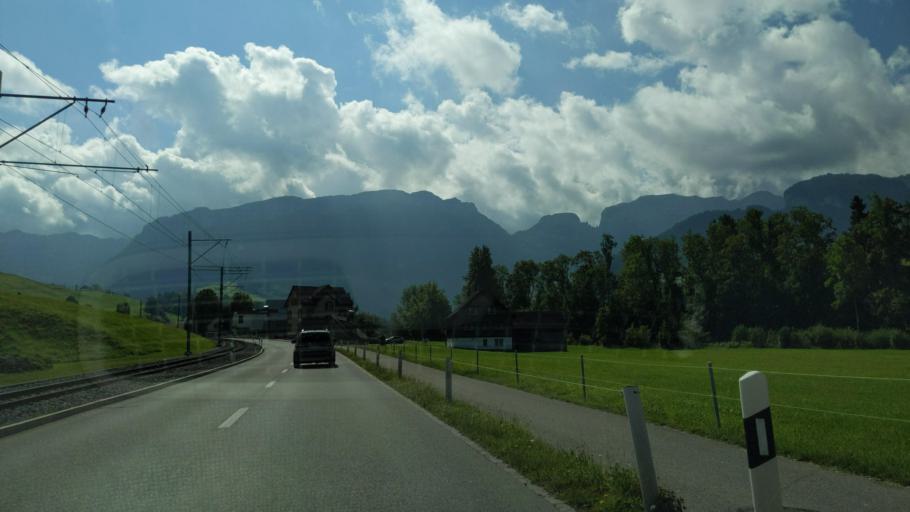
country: CH
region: Appenzell Innerrhoden
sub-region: Appenzell Inner Rhodes
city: Appenzell
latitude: 47.3163
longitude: 9.4339
